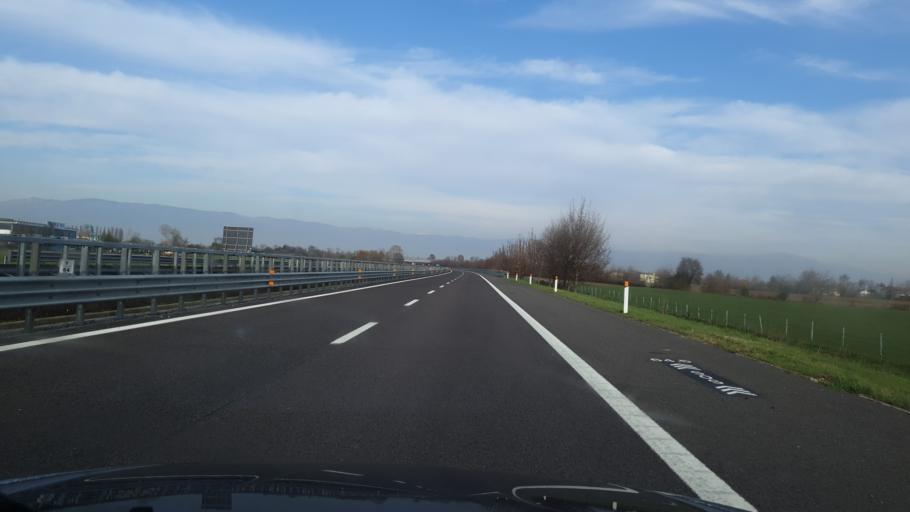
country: IT
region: Veneto
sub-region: Provincia di Vicenza
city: Vigardolo
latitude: 45.6039
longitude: 11.6003
